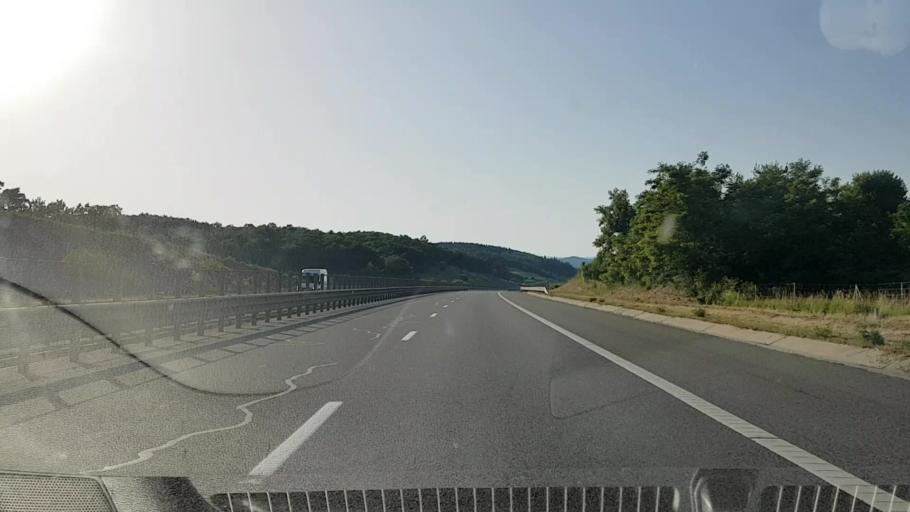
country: RO
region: Cluj
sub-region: Comuna Savadisla
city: Savadisla
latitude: 46.6641
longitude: 23.4929
